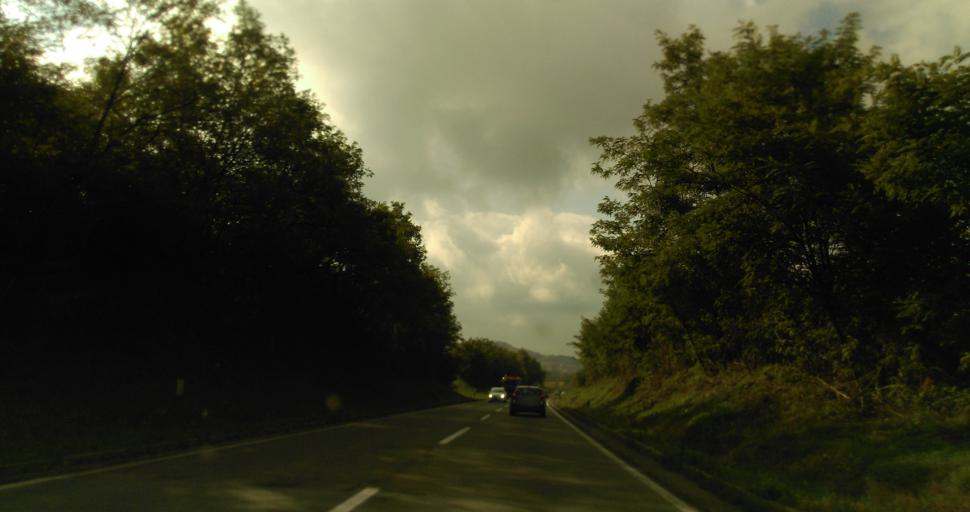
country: RS
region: Central Serbia
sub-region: Kolubarski Okrug
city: Ljig
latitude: 44.2570
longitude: 20.2864
